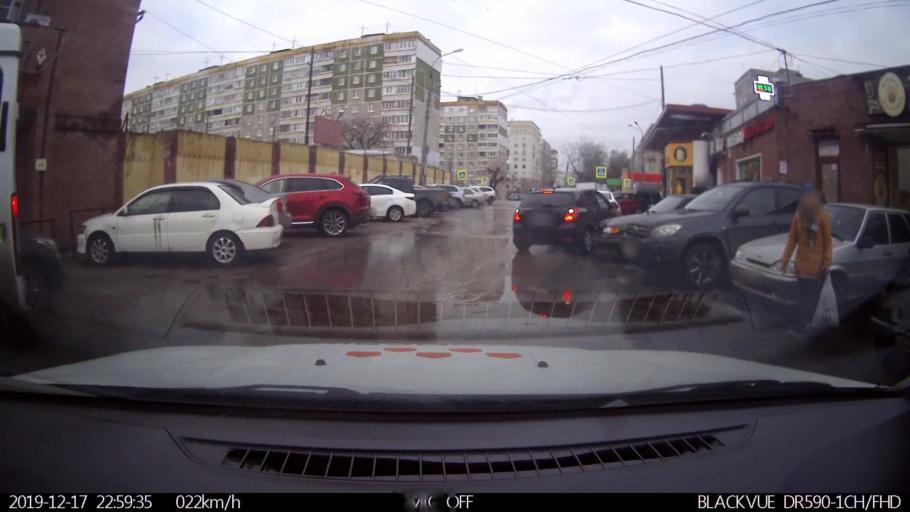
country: RU
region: Nizjnij Novgorod
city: Neklyudovo
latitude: 56.3526
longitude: 43.8594
